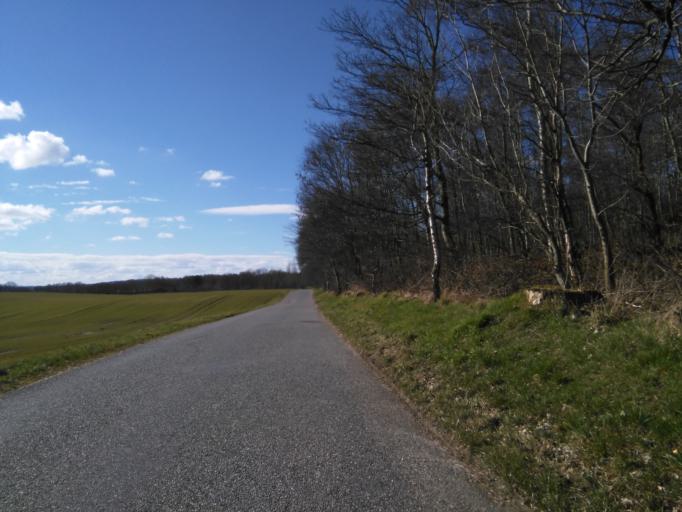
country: DK
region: Central Jutland
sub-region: Odder Kommune
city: Odder
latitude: 55.8911
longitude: 10.0163
